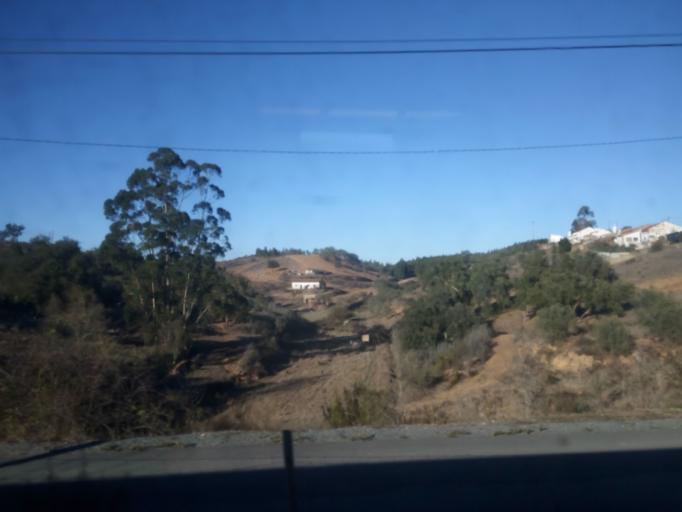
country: PT
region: Faro
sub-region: Monchique
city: Monchique
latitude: 37.4370
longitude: -8.4439
